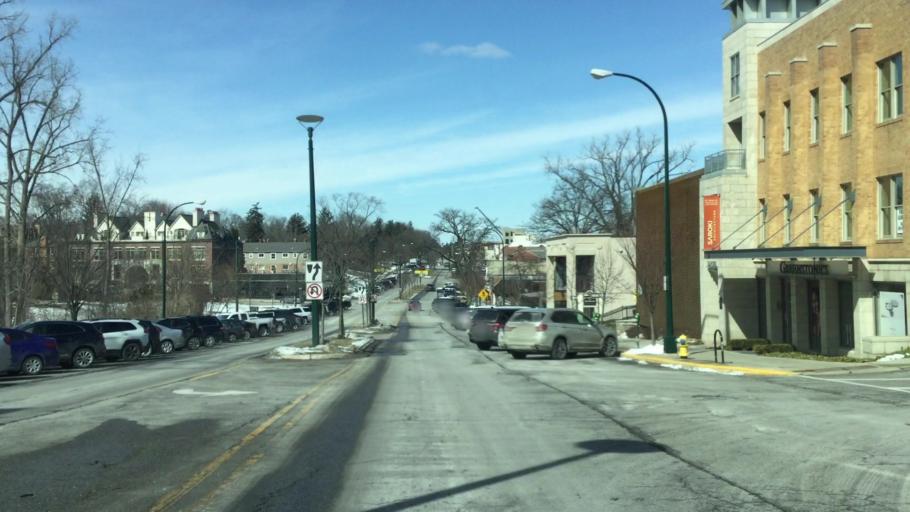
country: US
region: Michigan
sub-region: Oakland County
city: Birmingham
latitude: 42.5495
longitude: -83.2167
